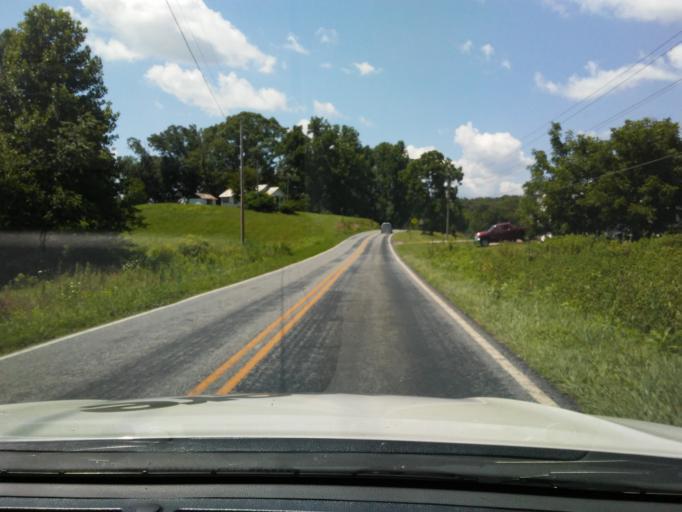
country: US
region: Georgia
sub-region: Towns County
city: Hiawassee
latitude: 34.9936
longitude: -83.7556
